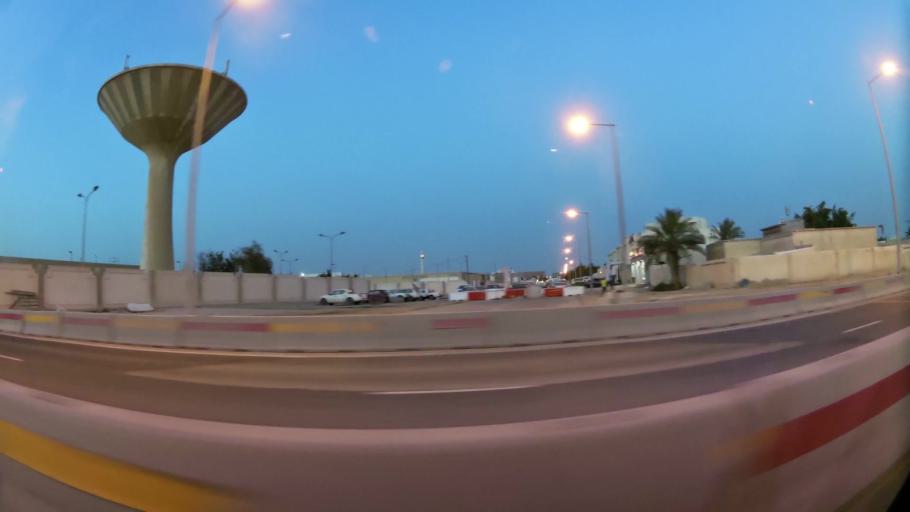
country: QA
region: Baladiyat ar Rayyan
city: Ar Rayyan
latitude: 25.3144
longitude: 51.4513
